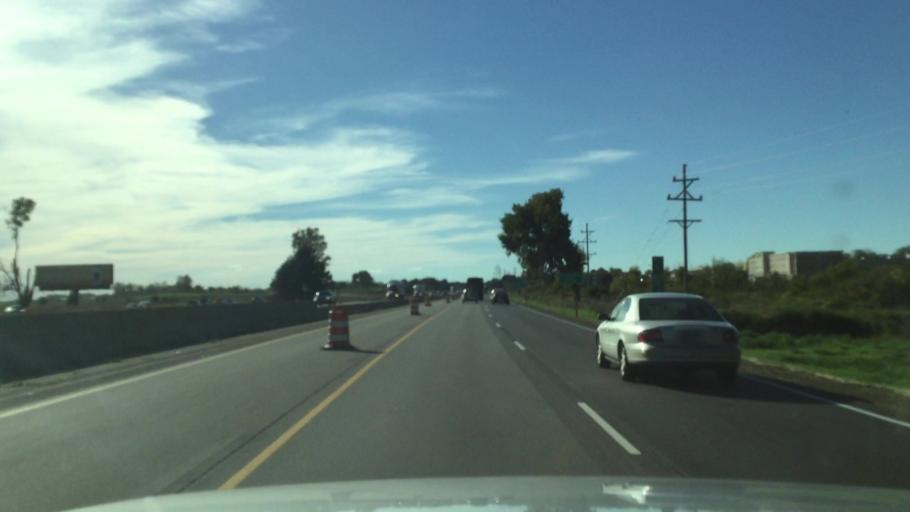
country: US
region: Michigan
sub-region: Jackson County
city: Jackson
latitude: 42.2690
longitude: -84.4421
